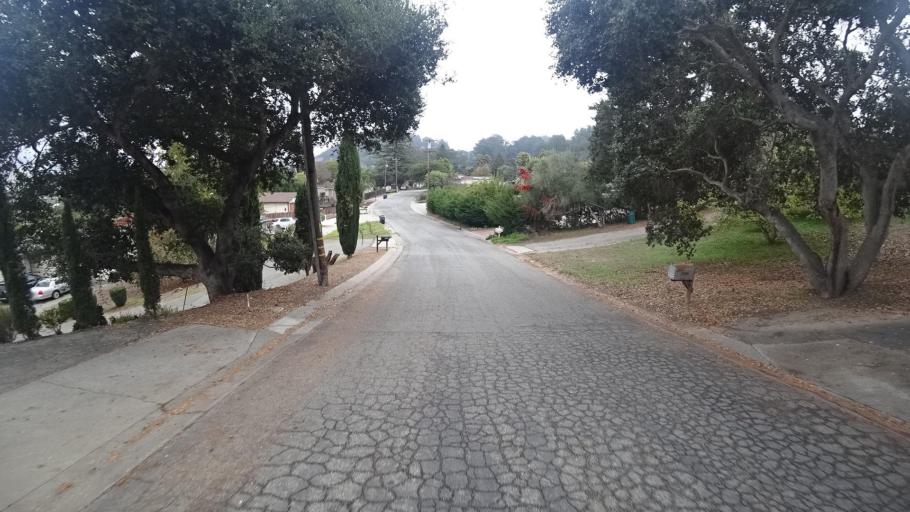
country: US
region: California
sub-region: San Benito County
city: Aromas
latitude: 36.8856
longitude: -121.6440
